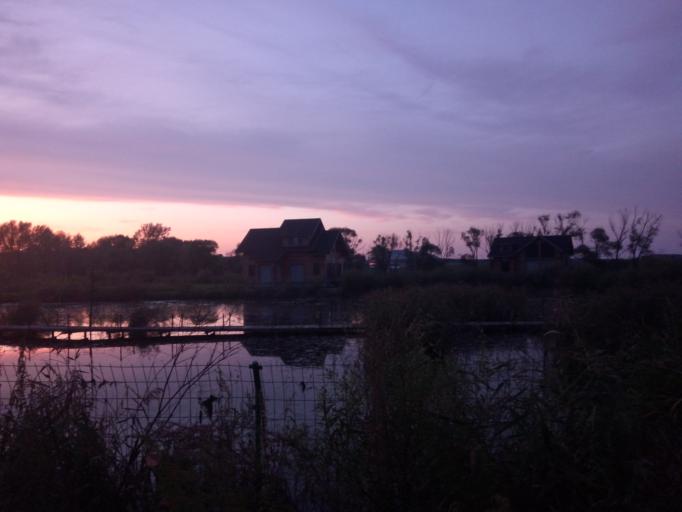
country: CN
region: Heilongjiang Sheng
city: Erjing
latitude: 48.6537
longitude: 126.1421
